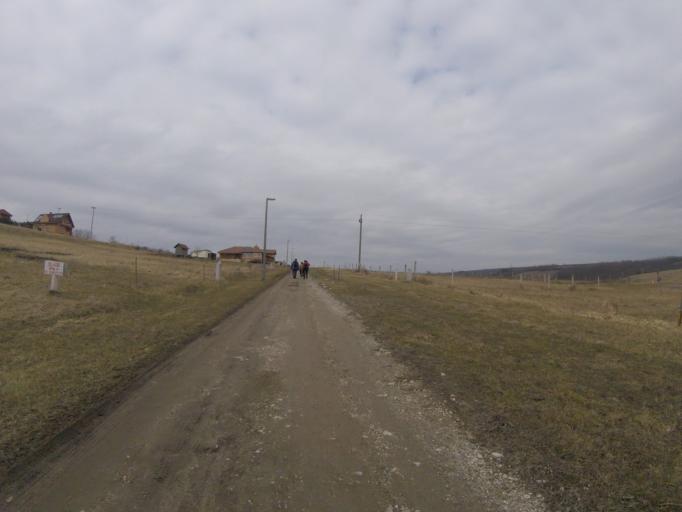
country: HU
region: Heves
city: Egerszalok
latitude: 47.8657
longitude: 20.3346
